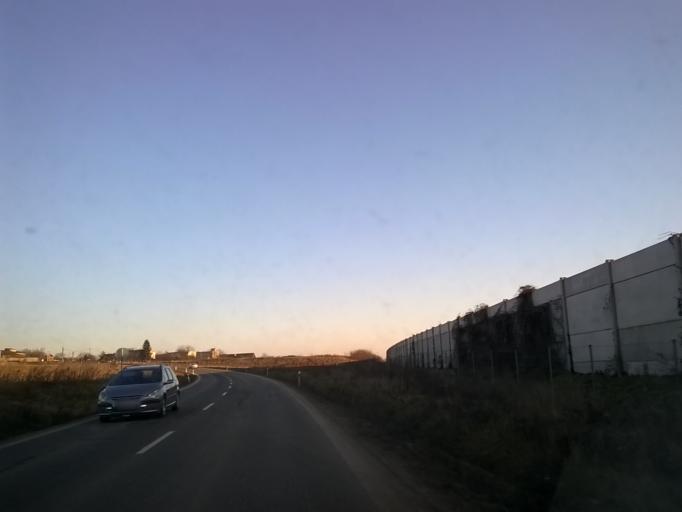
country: SK
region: Nitriansky
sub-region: Okres Nitra
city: Nitra
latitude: 48.2950
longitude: 18.0370
